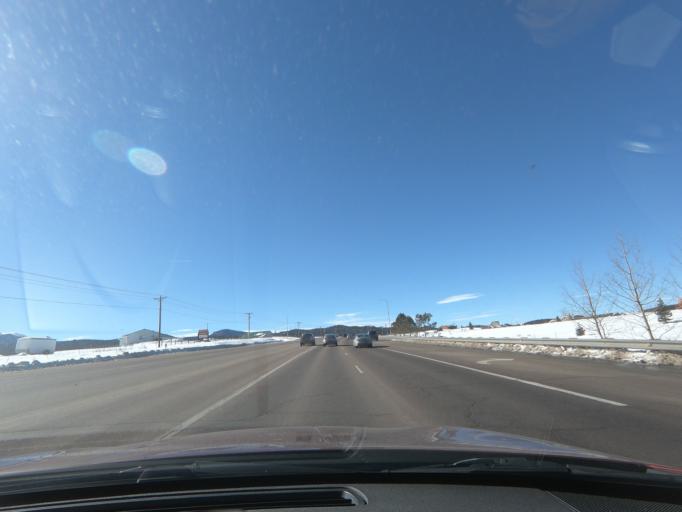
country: US
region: Colorado
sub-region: Teller County
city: Woodland Park
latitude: 38.9641
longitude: -105.0860
